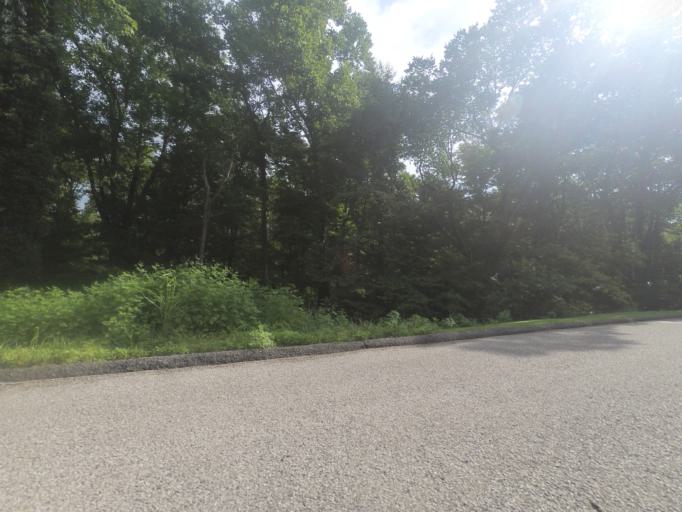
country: US
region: West Virginia
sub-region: Cabell County
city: Huntington
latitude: 38.3967
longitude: -82.4089
